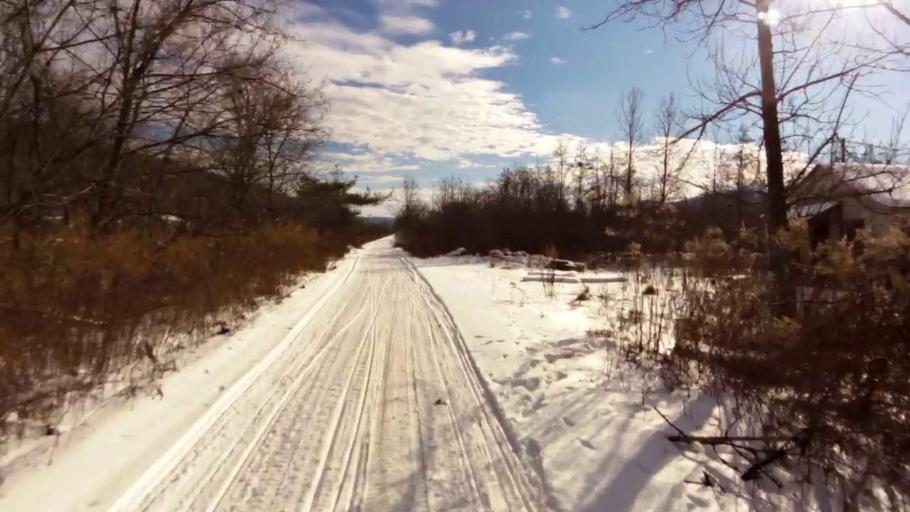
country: US
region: Pennsylvania
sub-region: McKean County
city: Foster Brook
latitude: 42.0227
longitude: -78.6301
